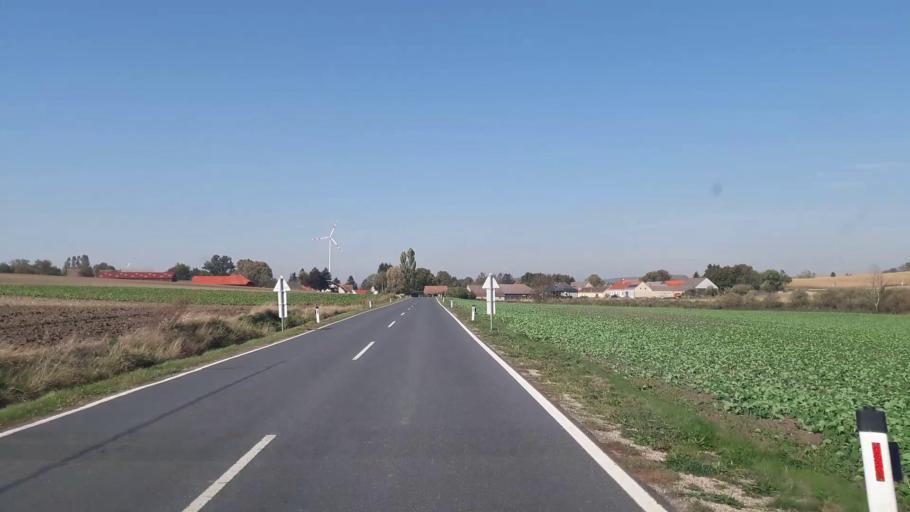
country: AT
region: Lower Austria
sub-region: Politischer Bezirk Korneuburg
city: Ernstbrunn
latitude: 48.4925
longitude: 16.3686
